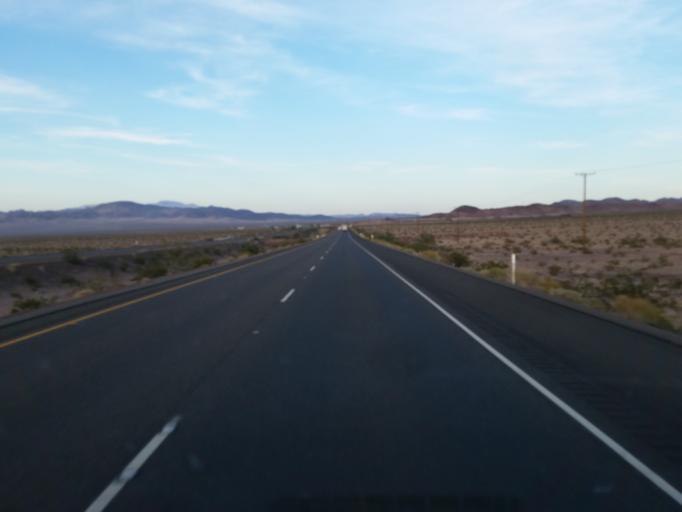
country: US
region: California
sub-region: San Bernardino County
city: Joshua Tree
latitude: 34.7244
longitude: -116.2065
